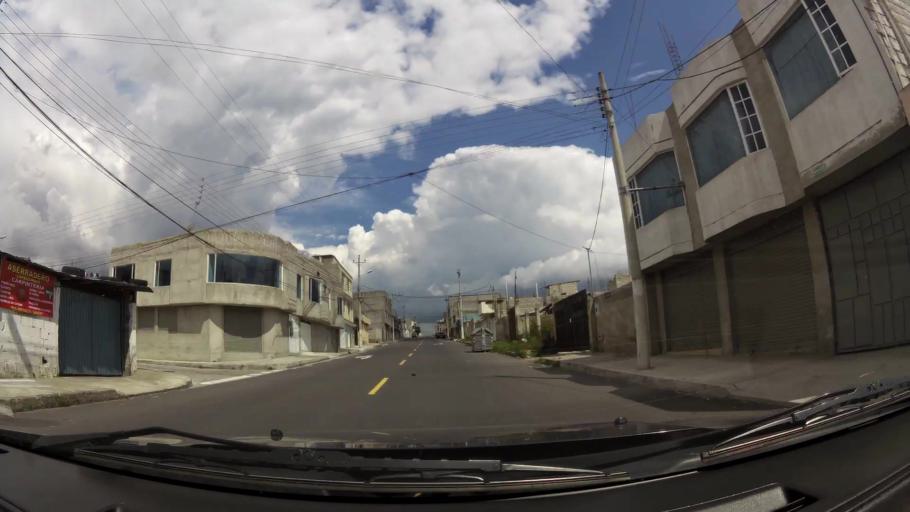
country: EC
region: Pichincha
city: Quito
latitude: -0.0924
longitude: -78.4557
